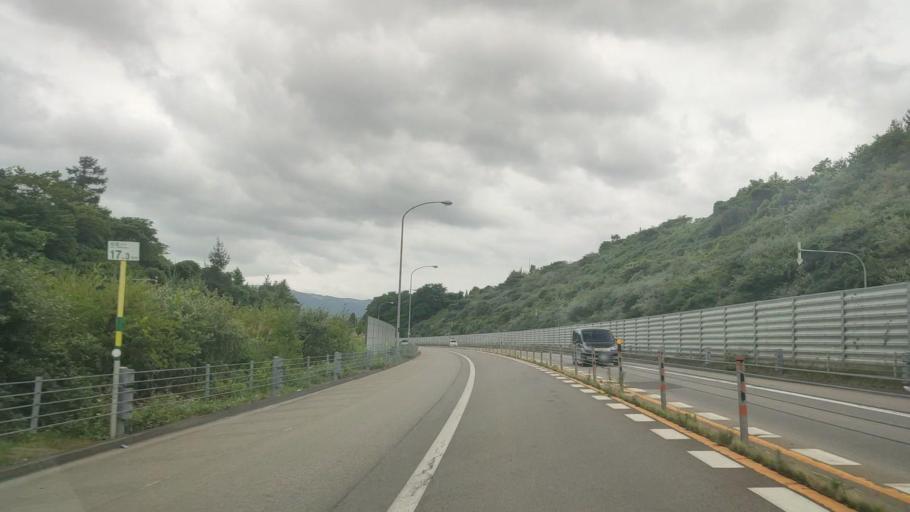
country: JP
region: Hokkaido
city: Nanae
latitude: 41.9139
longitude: 140.6904
